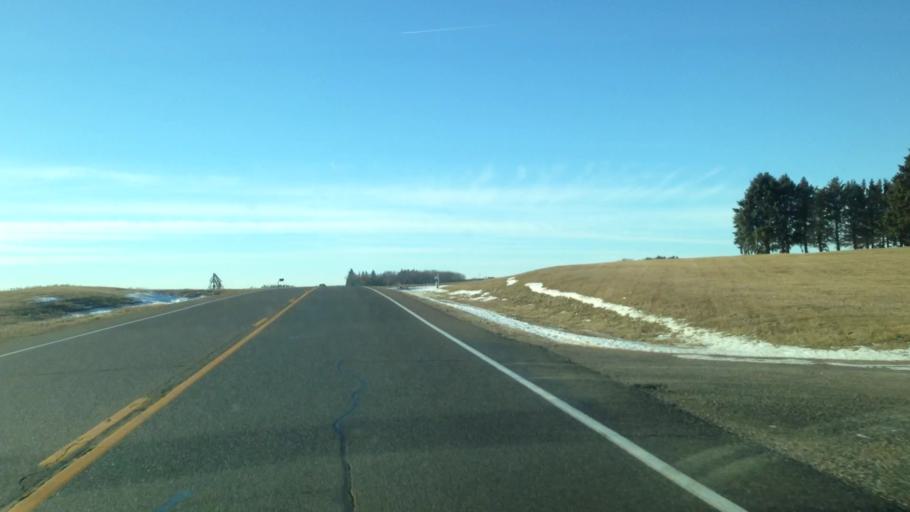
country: US
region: Minnesota
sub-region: Dakota County
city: Farmington
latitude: 44.5765
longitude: -93.0278
